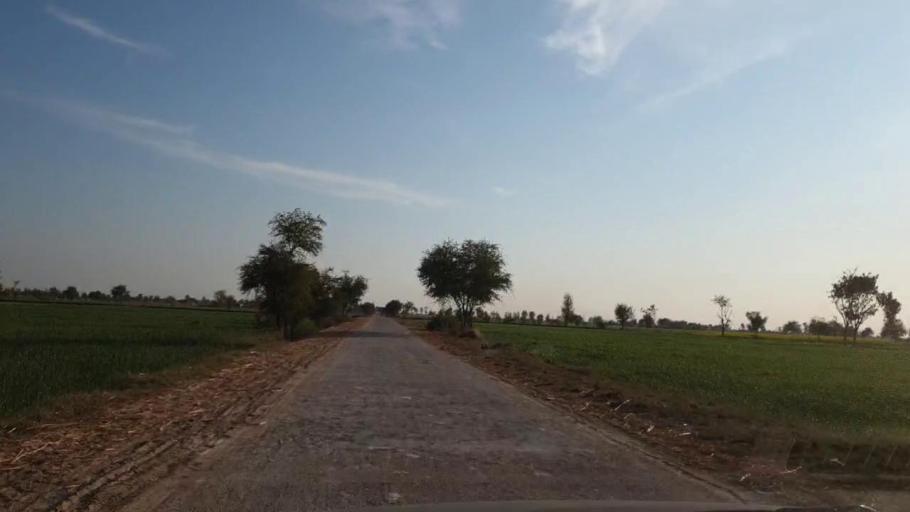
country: PK
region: Sindh
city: Khadro
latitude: 26.1982
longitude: 68.7469
